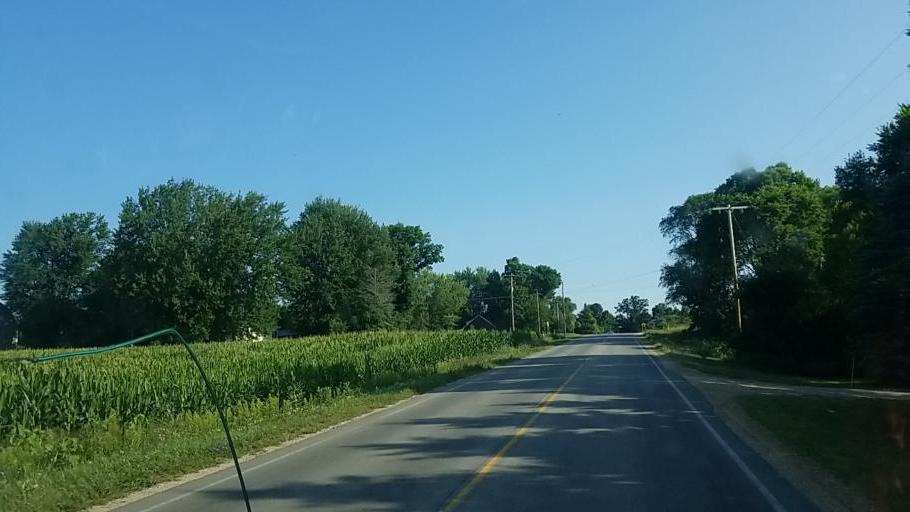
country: US
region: Michigan
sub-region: Newaygo County
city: Fremont
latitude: 43.4226
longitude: -85.9397
